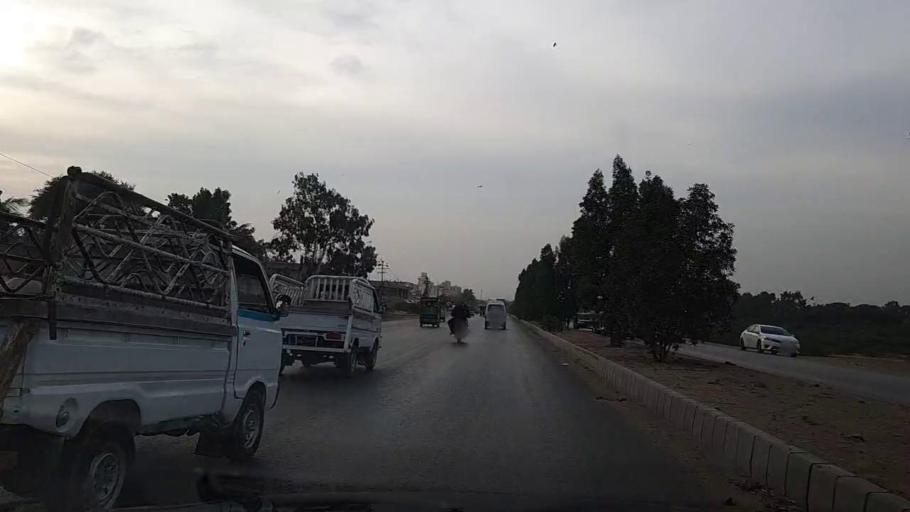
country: PK
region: Sindh
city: Malir Cantonment
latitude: 24.8594
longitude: 67.3392
